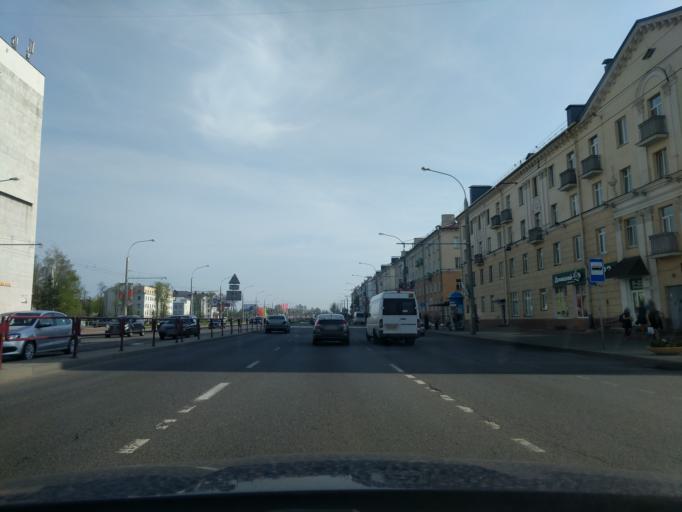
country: BY
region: Minsk
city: Minsk
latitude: 53.8636
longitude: 27.5711
